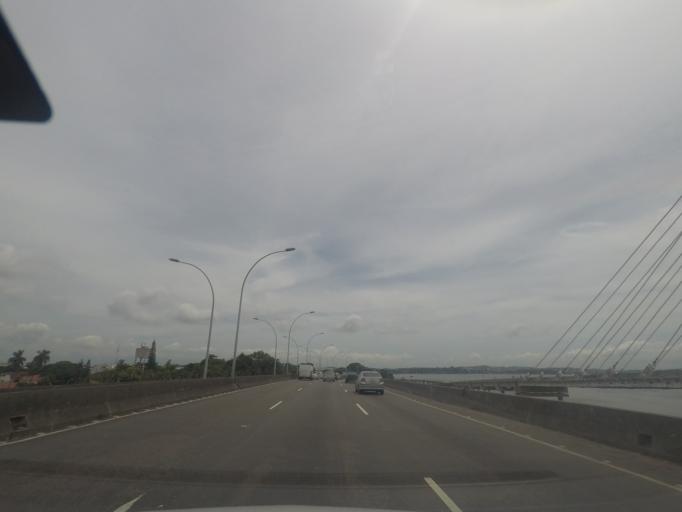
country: BR
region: Rio de Janeiro
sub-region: Rio De Janeiro
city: Rio de Janeiro
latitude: -22.8352
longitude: -43.2406
